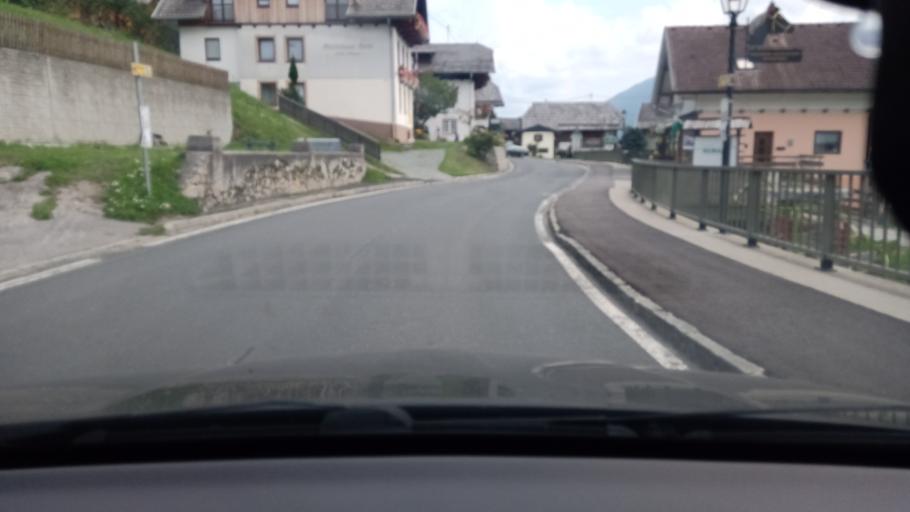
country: AT
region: Carinthia
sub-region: Politischer Bezirk Spittal an der Drau
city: Steinfeld
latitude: 46.7180
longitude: 13.2911
